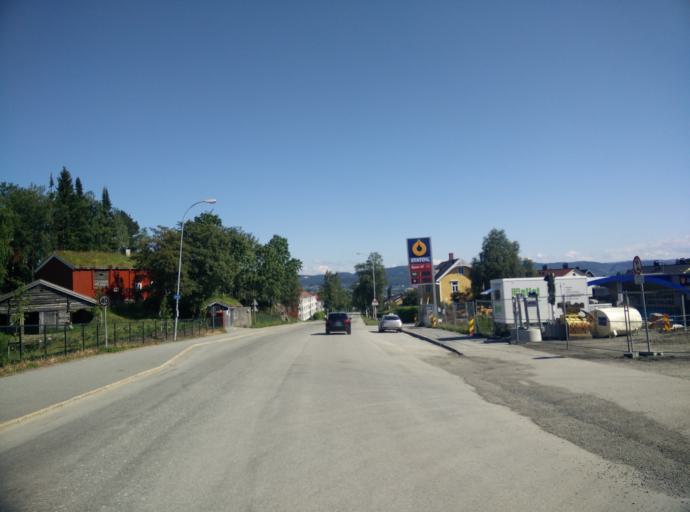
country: NO
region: Sor-Trondelag
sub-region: Trondheim
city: Trondheim
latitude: 63.4176
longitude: 10.3539
